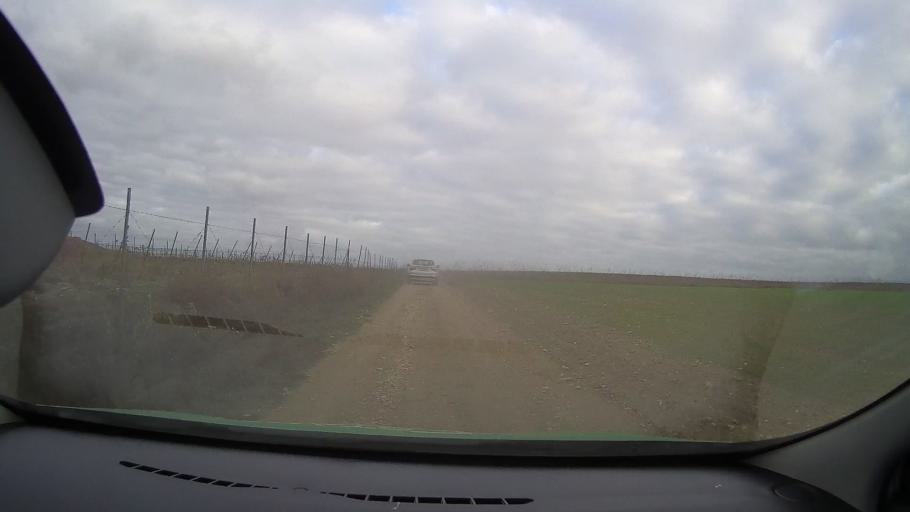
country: RO
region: Tulcea
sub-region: Comuna Jurilovca
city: Jurilovca
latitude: 44.7693
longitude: 28.9067
